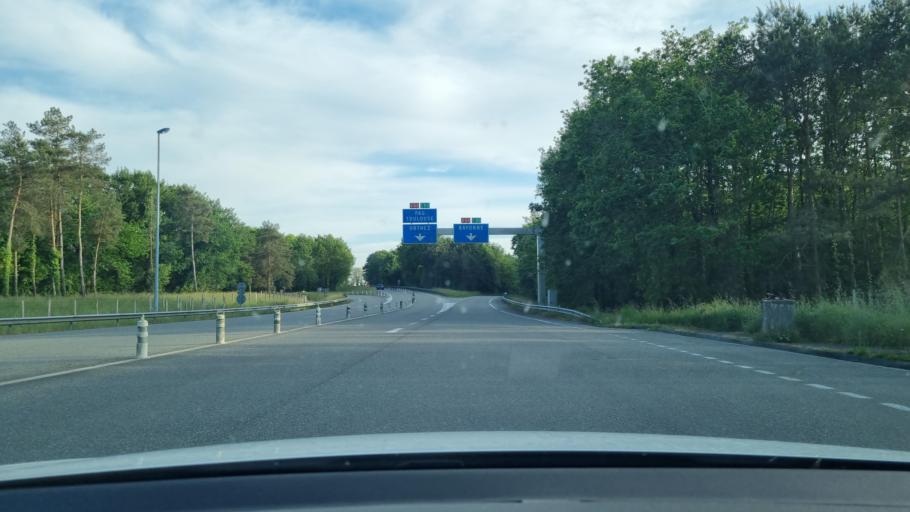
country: FR
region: Aquitaine
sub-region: Departement des Landes
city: Peyrehorade
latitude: 43.5167
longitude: -1.1040
